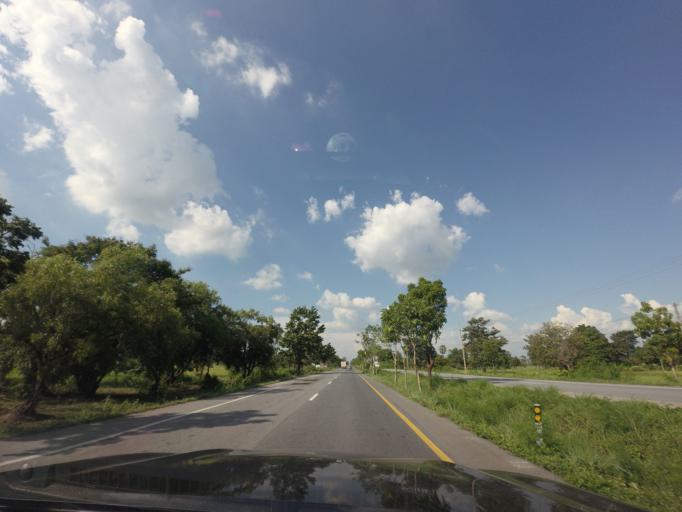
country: TH
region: Nakhon Ratchasima
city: Bua Lai
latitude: 15.7120
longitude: 102.5883
